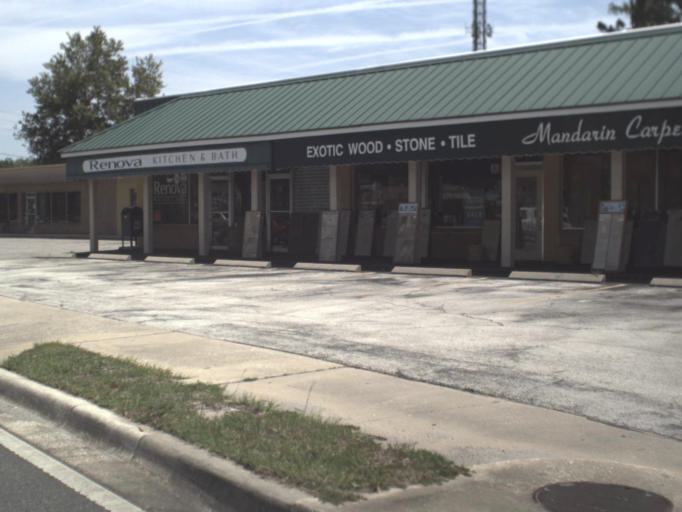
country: US
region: Florida
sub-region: Saint Johns County
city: Fruit Cove
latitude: 30.1654
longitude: -81.6324
